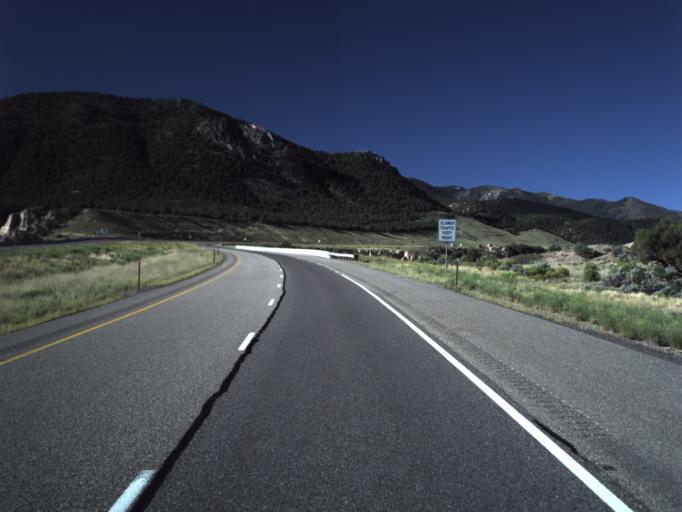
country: US
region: Utah
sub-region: Sevier County
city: Monroe
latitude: 38.5595
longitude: -112.3625
